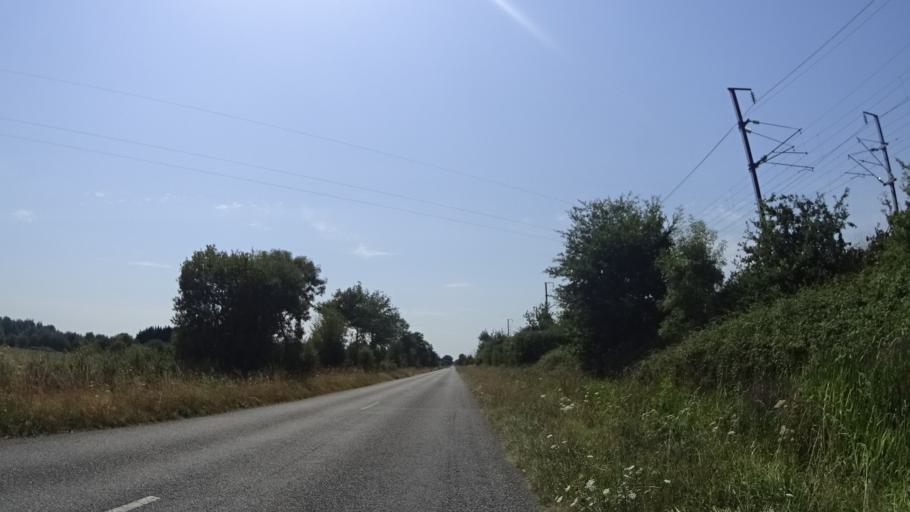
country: FR
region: Pays de la Loire
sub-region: Departement de la Loire-Atlantique
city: La Chapelle-Launay
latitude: 47.3588
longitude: -1.9708
